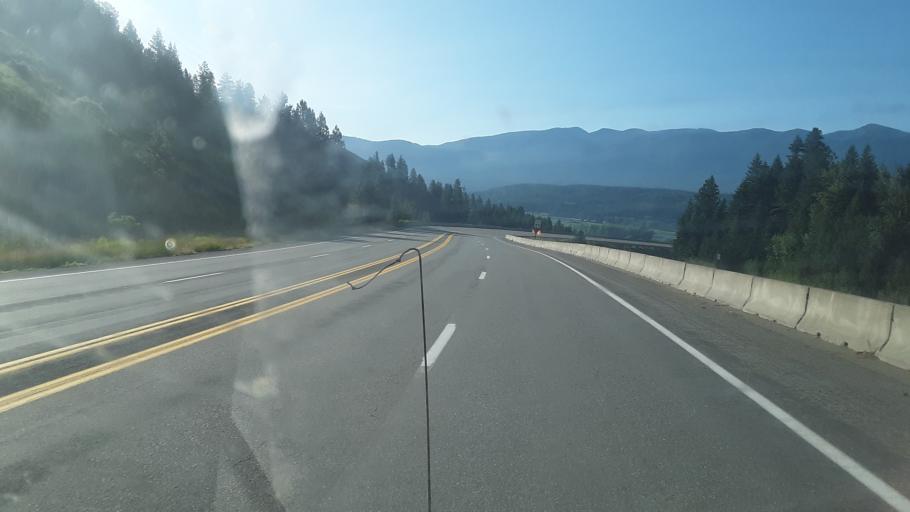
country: US
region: Idaho
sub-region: Boundary County
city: Bonners Ferry
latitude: 48.7147
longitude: -116.3071
